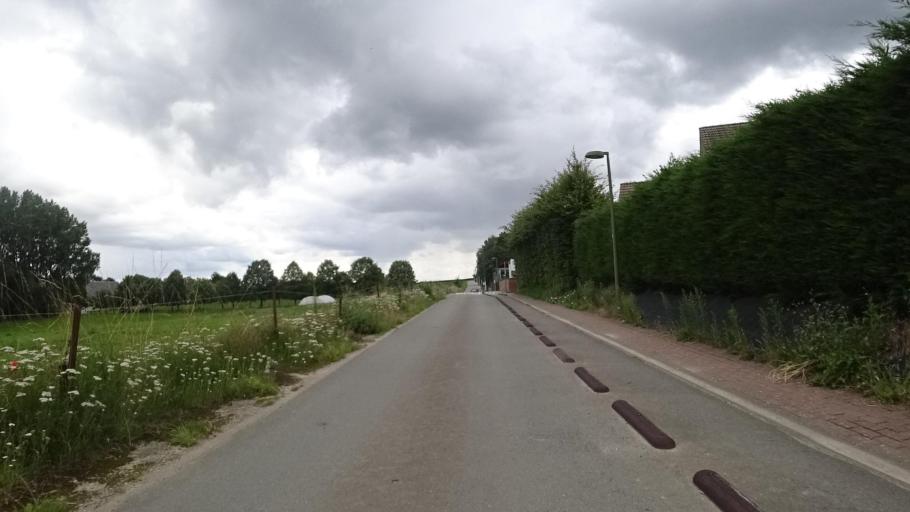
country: BE
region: Wallonia
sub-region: Province du Brabant Wallon
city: Chastre
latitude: 50.5810
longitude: 4.6002
